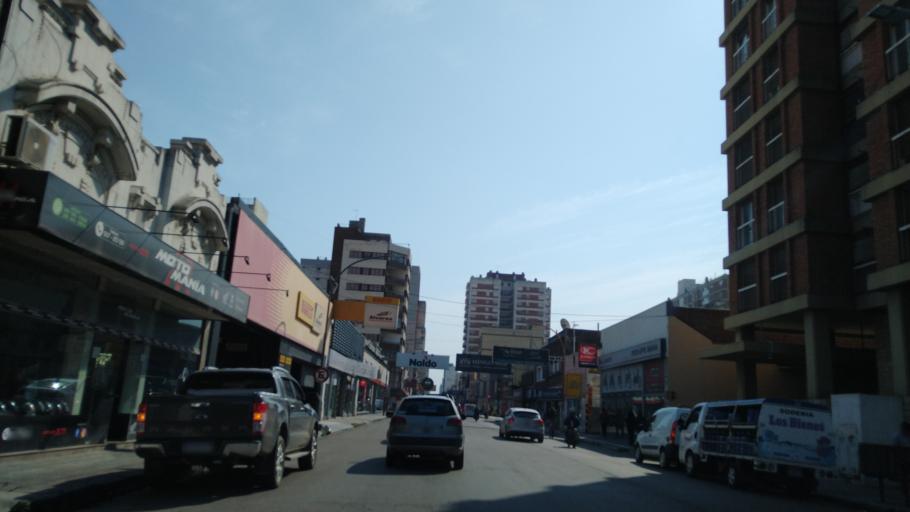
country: AR
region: Buenos Aires
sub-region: Partido de Bahia Blanca
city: Bahia Blanca
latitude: -38.7231
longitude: -62.2641
